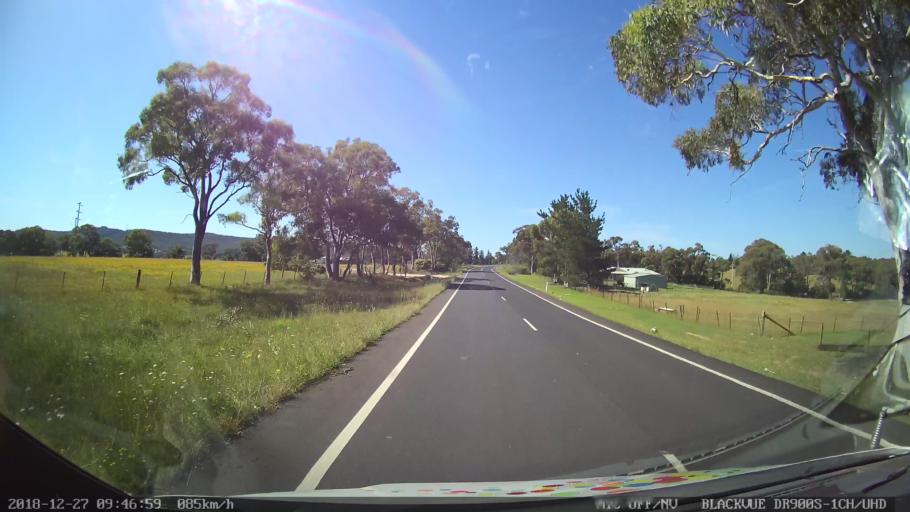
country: AU
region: New South Wales
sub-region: Lithgow
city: Portland
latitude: -33.3410
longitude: 149.9884
